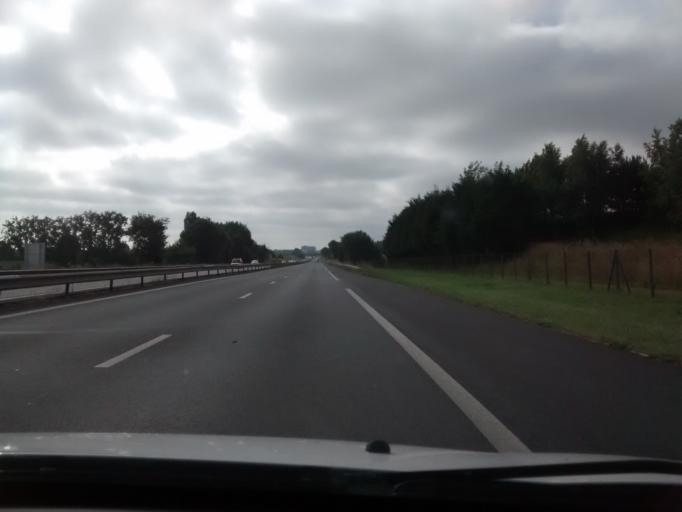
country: FR
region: Brittany
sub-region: Departement d'Ille-et-Vilaine
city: Chateaubourg
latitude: 48.0981
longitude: -1.4124
